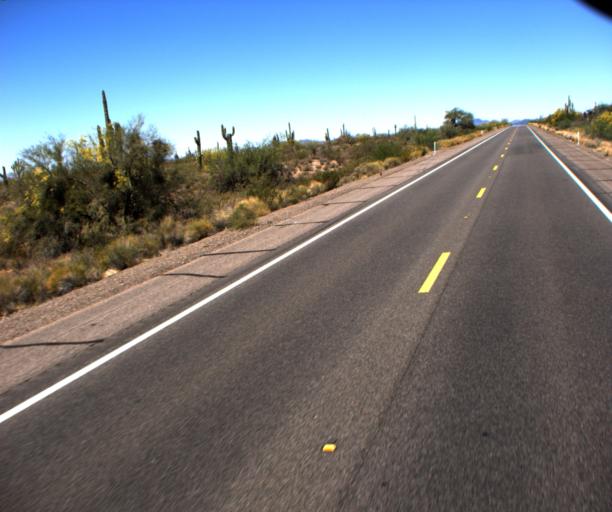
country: US
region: Arizona
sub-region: Maricopa County
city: Wickenburg
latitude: 33.8481
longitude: -112.5354
